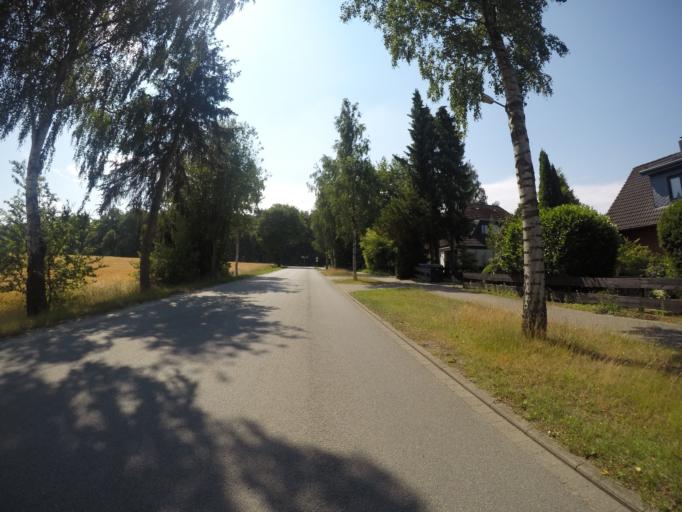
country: DE
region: Lower Saxony
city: Buchholz in der Nordheide
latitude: 53.3104
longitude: 9.8223
